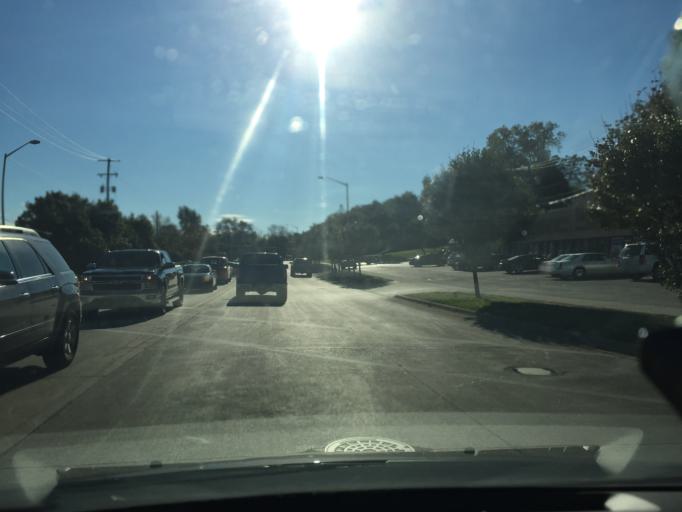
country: US
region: Michigan
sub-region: Oakland County
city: Pontiac
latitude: 42.6490
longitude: -83.2710
